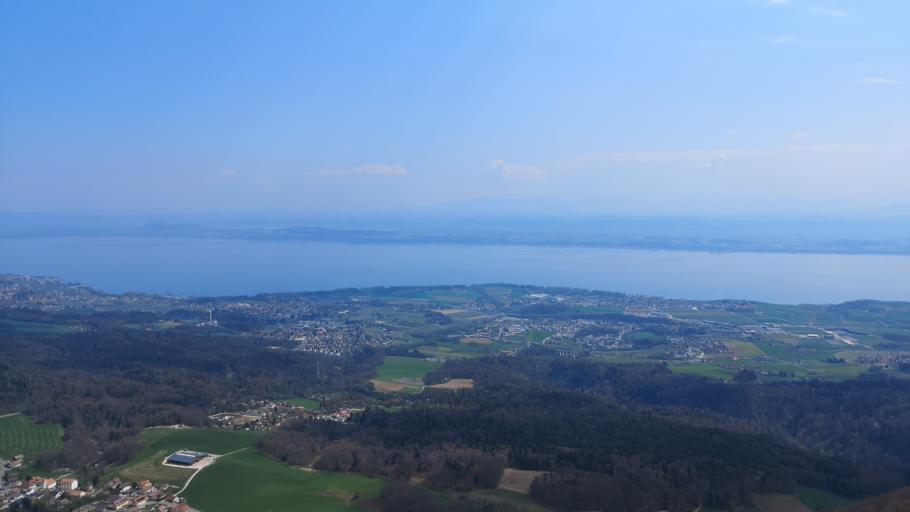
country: CH
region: Neuchatel
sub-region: Boudry District
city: Bevaix
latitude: 46.9767
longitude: 6.7918
